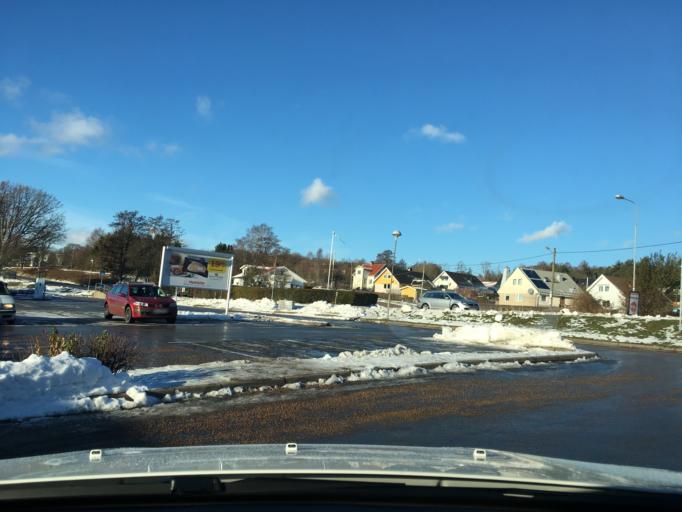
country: SE
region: Vaestra Goetaland
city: Svanesund
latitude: 58.1427
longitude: 11.8215
